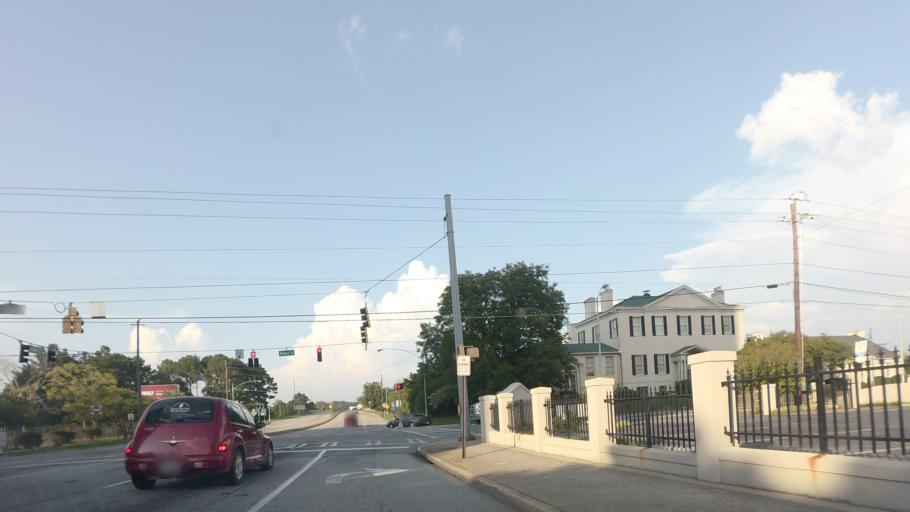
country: US
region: Georgia
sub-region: Bibb County
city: Macon
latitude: 32.8389
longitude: -83.6270
